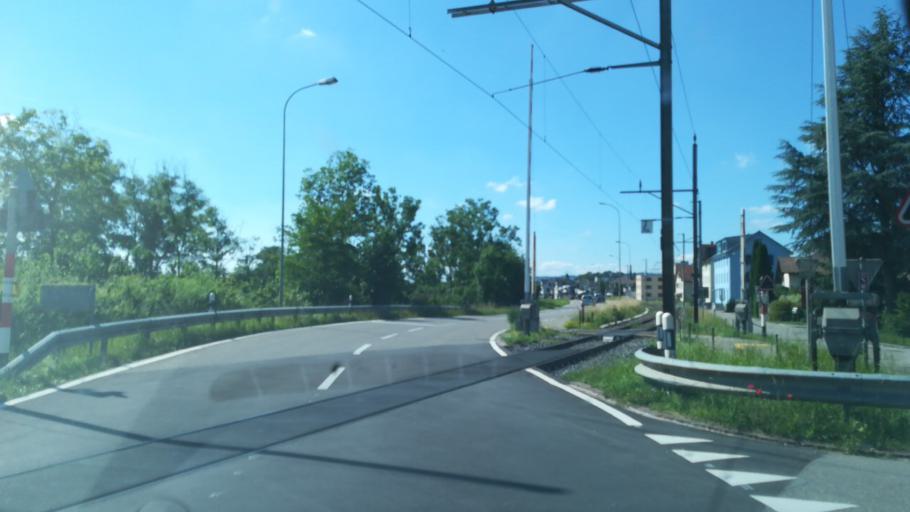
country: CH
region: Thurgau
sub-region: Weinfelden District
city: Sulgen
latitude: 47.5209
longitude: 9.2072
